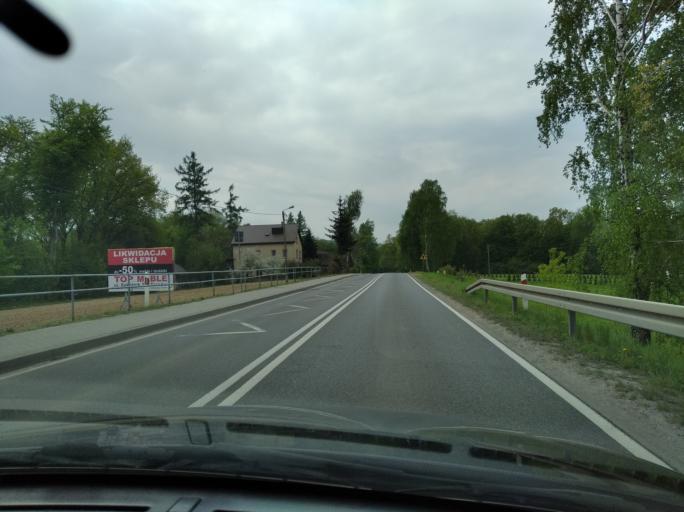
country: PL
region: Lesser Poland Voivodeship
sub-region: Powiat tarnowski
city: Tarnowiec
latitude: 49.9636
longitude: 20.9925
